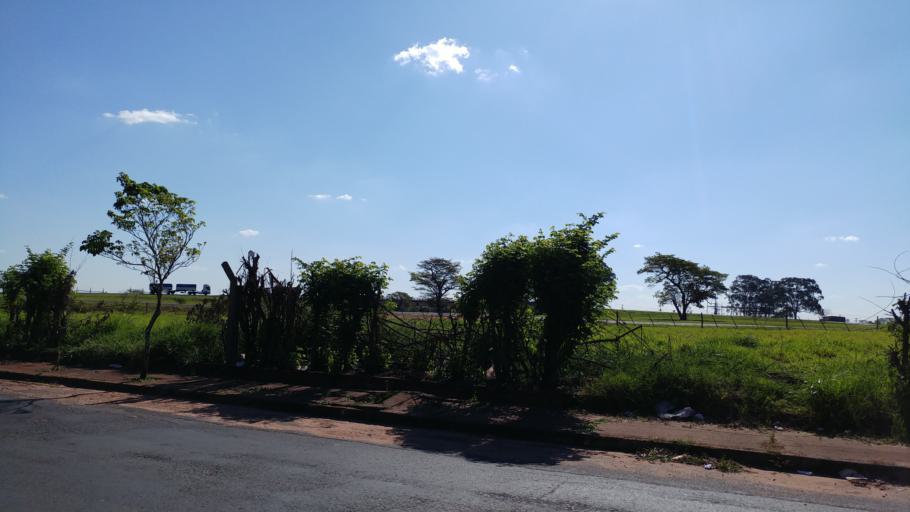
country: BR
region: Sao Paulo
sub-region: Paraguacu Paulista
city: Paraguacu Paulista
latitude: -22.4334
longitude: -50.5852
